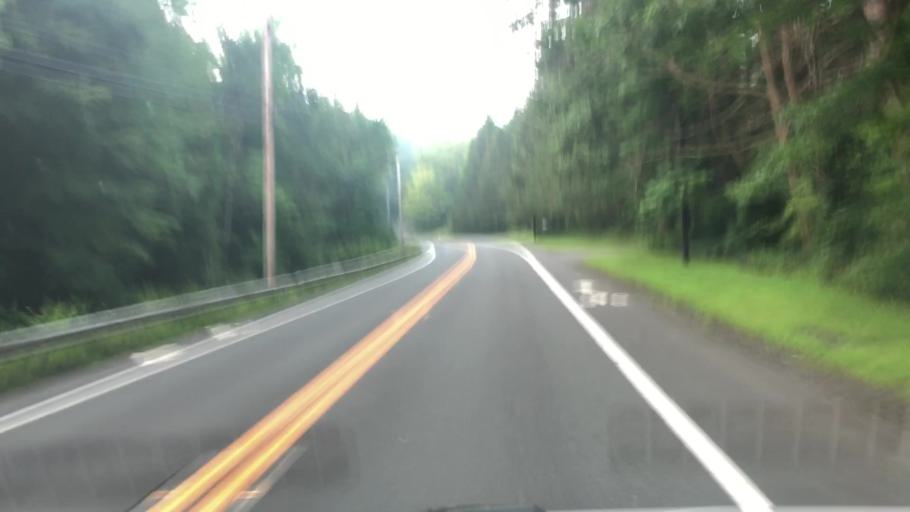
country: US
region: Massachusetts
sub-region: Franklin County
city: Buckland
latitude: 42.5619
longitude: -72.8043
